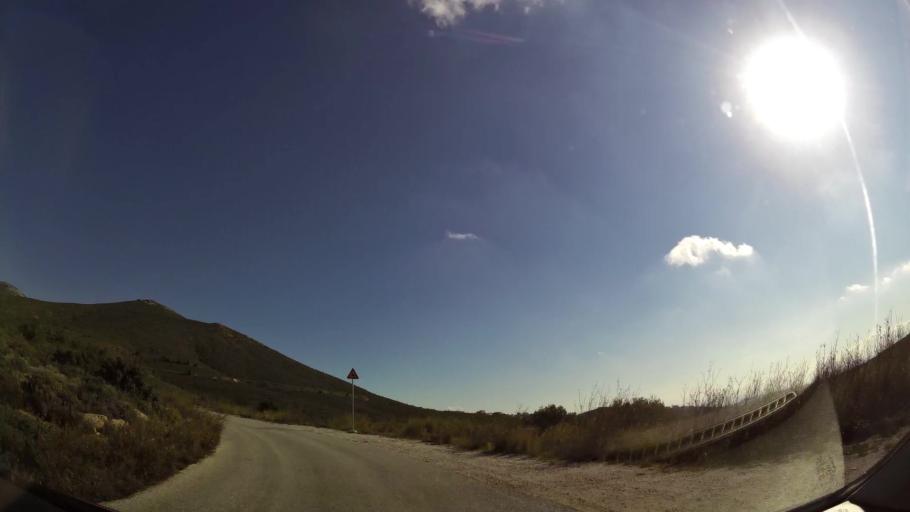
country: GR
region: Attica
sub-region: Nomarchia Anatolikis Attikis
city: Dhrafi
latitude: 38.0392
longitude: 23.9117
